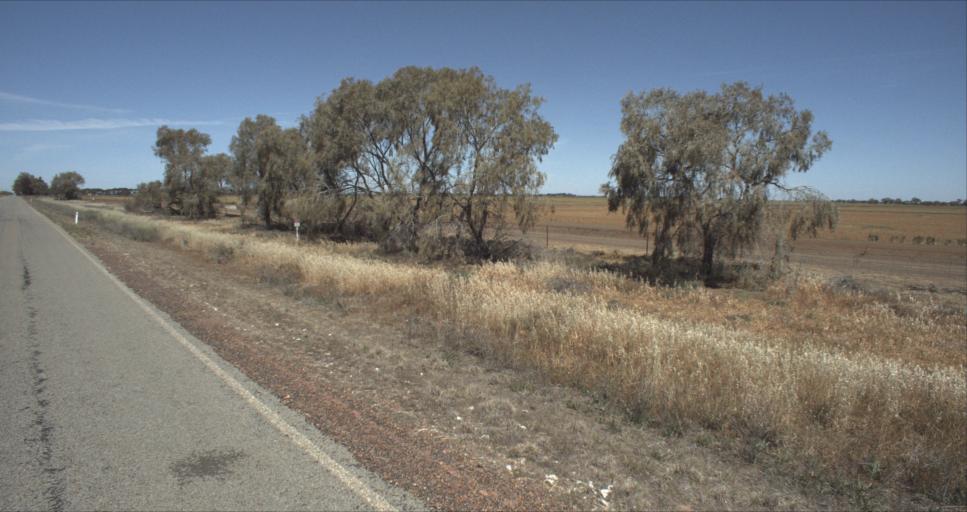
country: AU
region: New South Wales
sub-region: Leeton
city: Leeton
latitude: -34.4606
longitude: 146.2942
